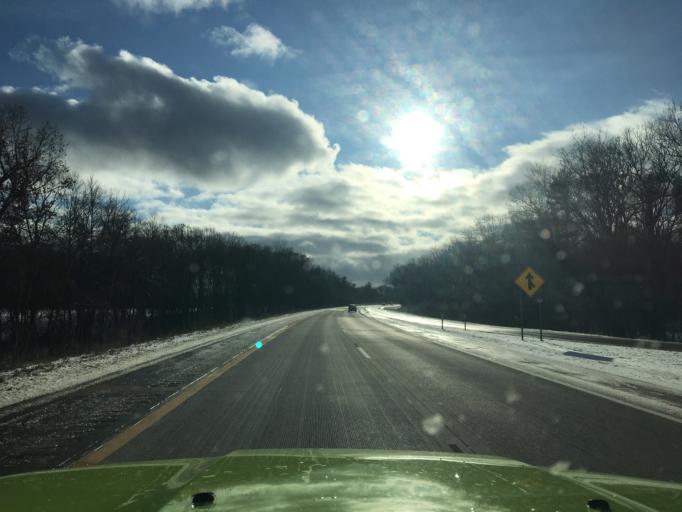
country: US
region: Michigan
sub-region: Kent County
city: Rockford
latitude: 43.1370
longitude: -85.5916
